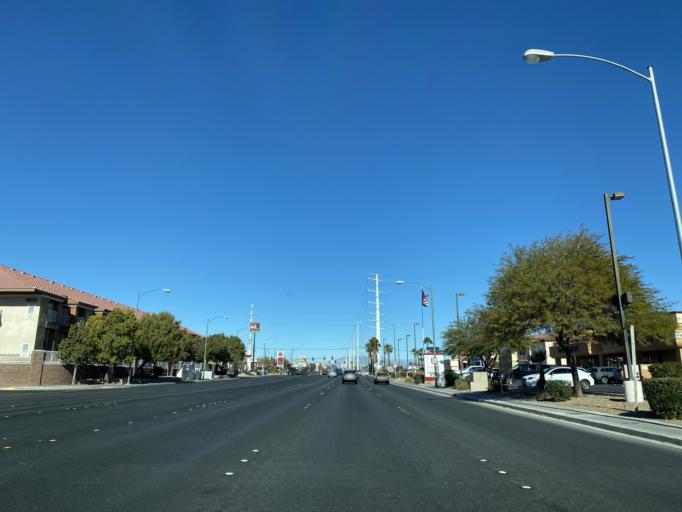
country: US
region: Nevada
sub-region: Clark County
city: Spring Valley
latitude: 36.1126
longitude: -115.2790
